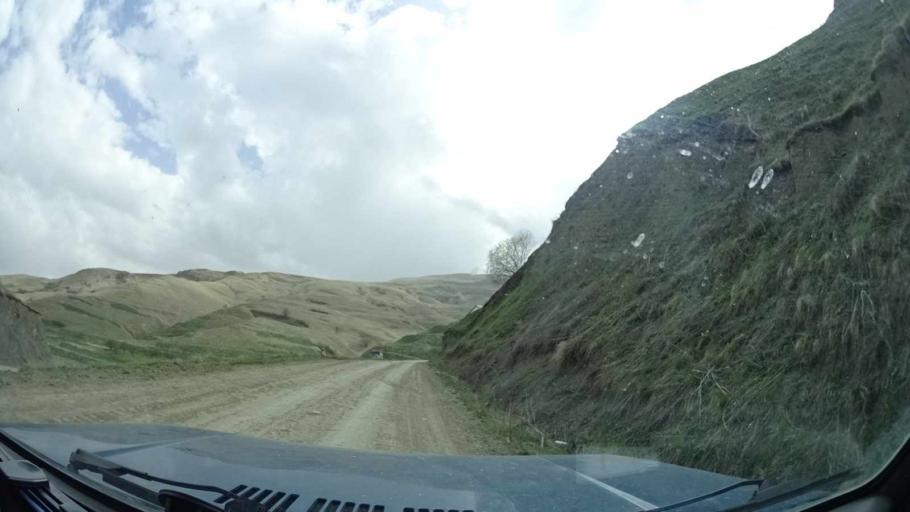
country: RU
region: Dagestan
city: Usisha
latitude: 42.1336
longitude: 47.3676
